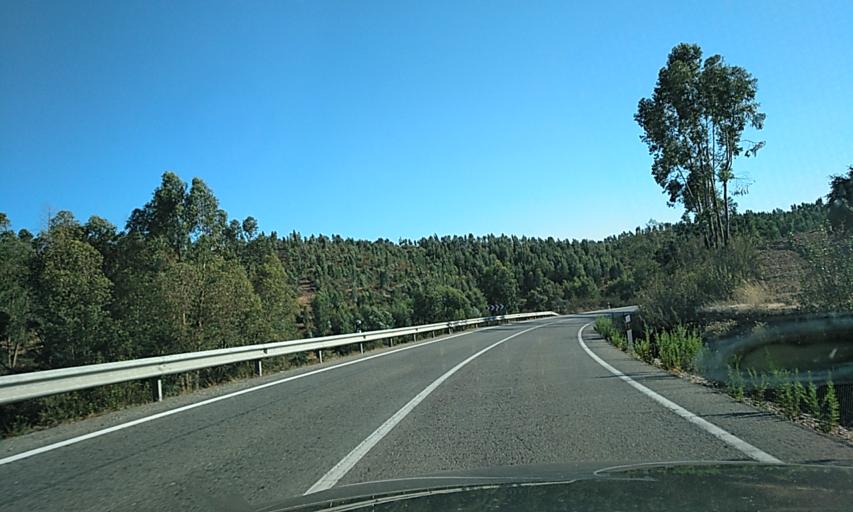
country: ES
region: Andalusia
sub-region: Provincia de Huelva
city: Santa Barbara de Casa
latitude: 37.8265
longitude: -7.2071
